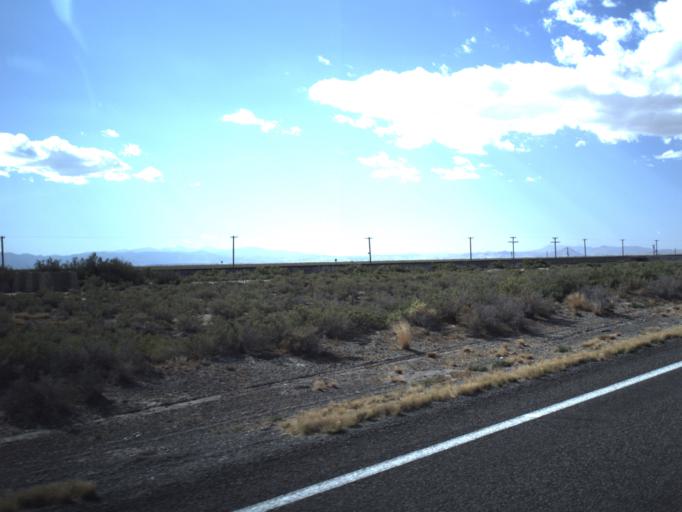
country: US
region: Utah
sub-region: Millard County
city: Delta
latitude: 39.1213
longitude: -112.7378
